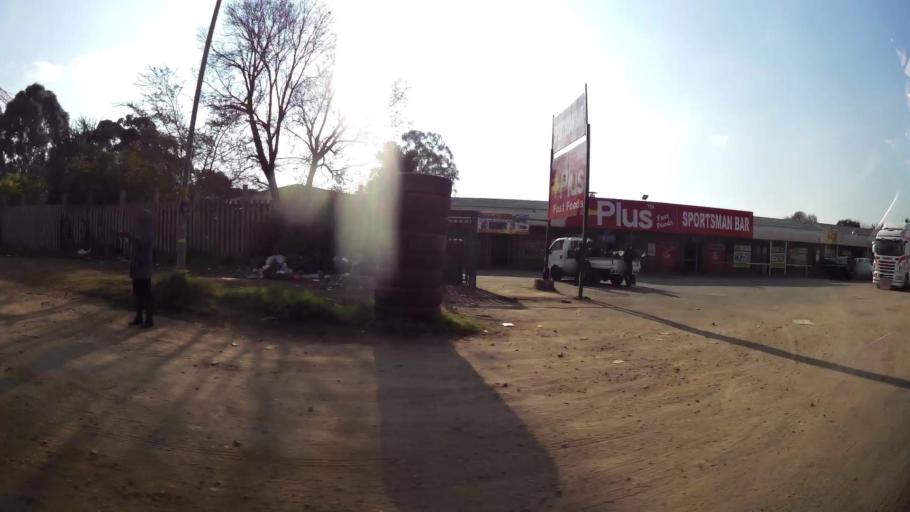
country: ZA
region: Gauteng
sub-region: Ekurhuleni Metropolitan Municipality
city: Tembisa
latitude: -26.0905
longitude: 28.2722
